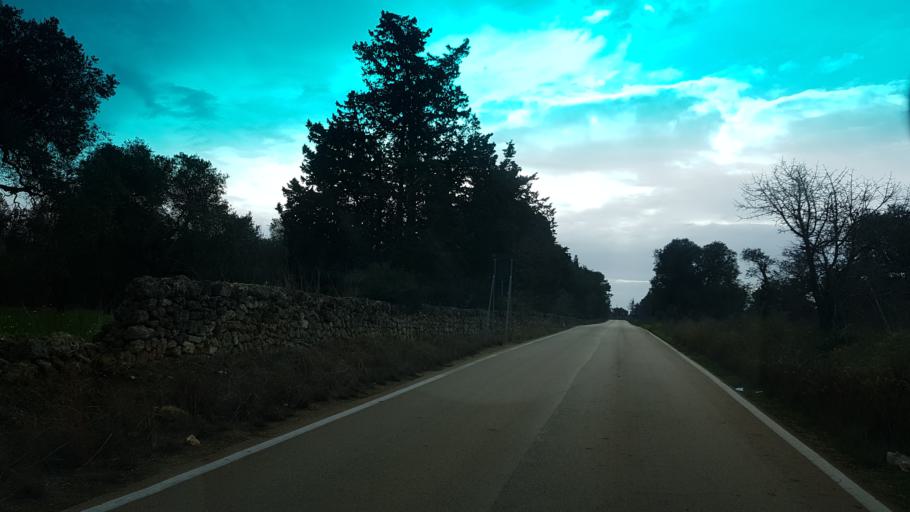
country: IT
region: Apulia
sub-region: Provincia di Brindisi
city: San Vito dei Normanni
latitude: 40.6983
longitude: 17.7596
